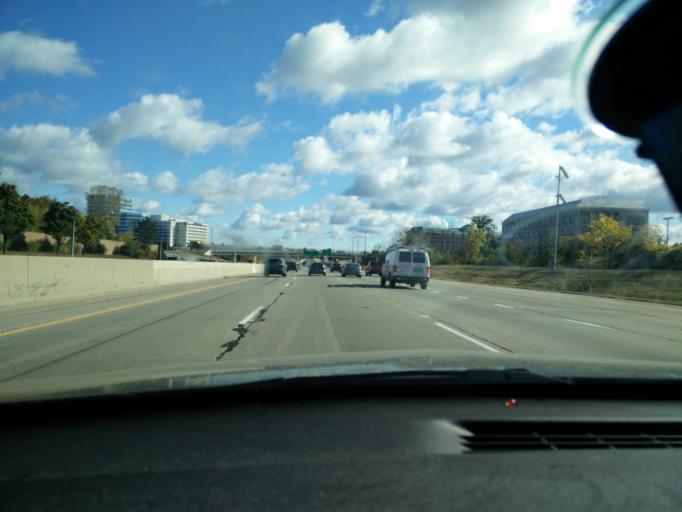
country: US
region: Michigan
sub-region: Oakland County
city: Franklin
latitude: 42.4922
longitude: -83.3043
